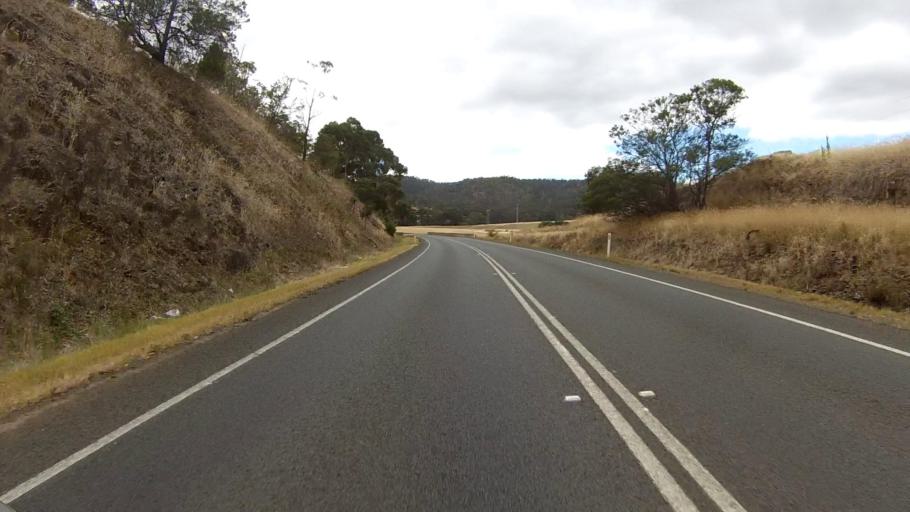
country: AU
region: Tasmania
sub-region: Sorell
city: Sorell
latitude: -42.7020
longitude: 147.5226
